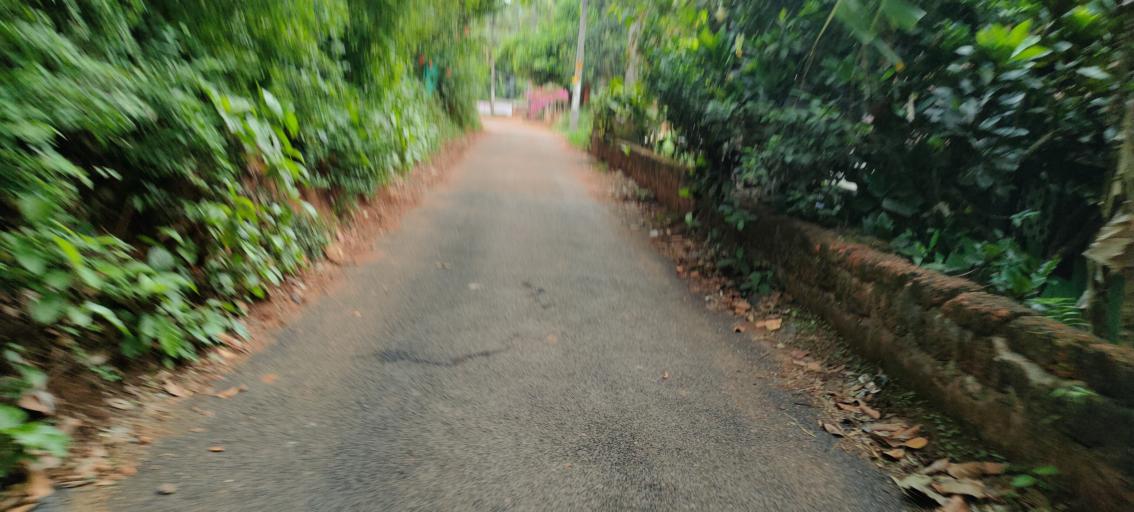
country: IN
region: Kerala
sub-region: Malappuram
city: Ponnani
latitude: 10.7723
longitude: 76.0313
